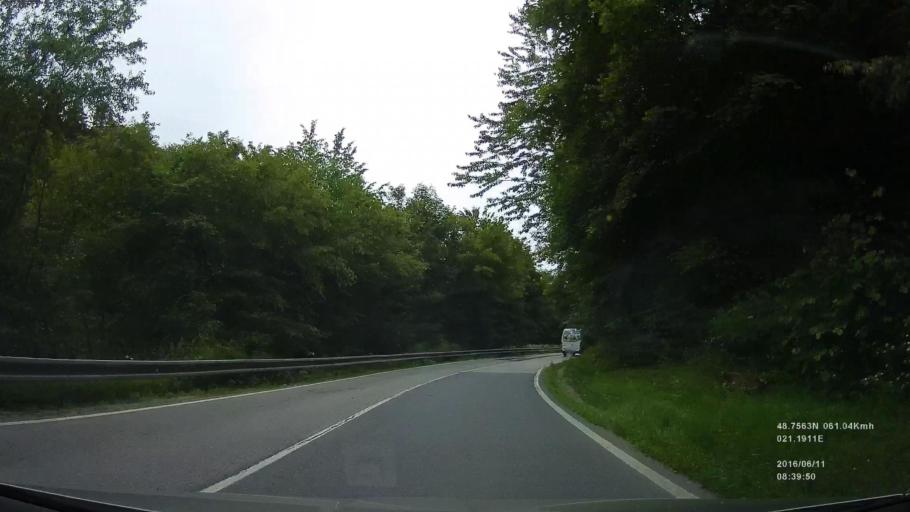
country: SK
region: Kosicky
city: Kosice
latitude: 48.7447
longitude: 21.2367
